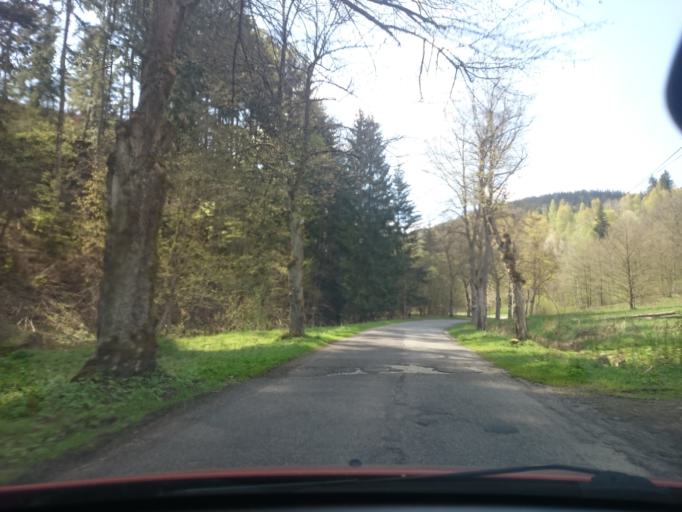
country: PL
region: Lower Silesian Voivodeship
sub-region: Powiat klodzki
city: Polanica-Zdroj
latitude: 50.3030
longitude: 16.5331
